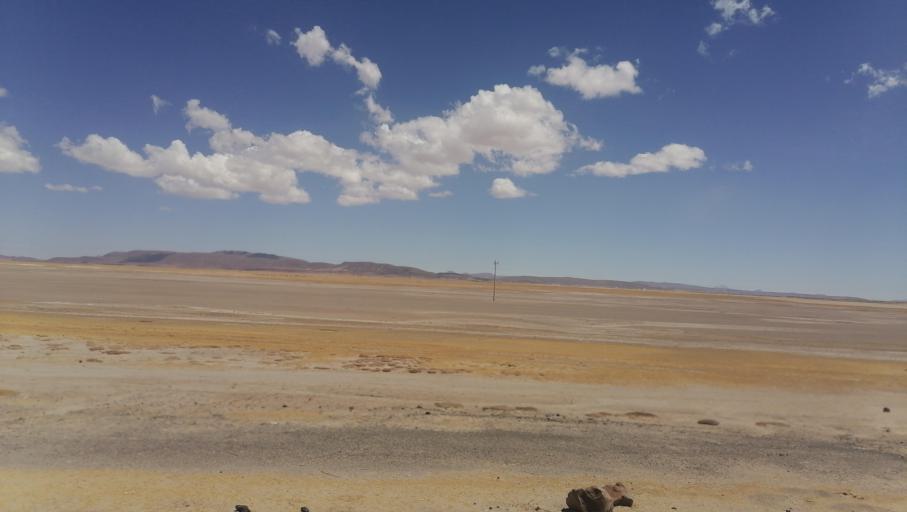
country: BO
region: Oruro
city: Challapata
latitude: -19.2148
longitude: -67.0198
